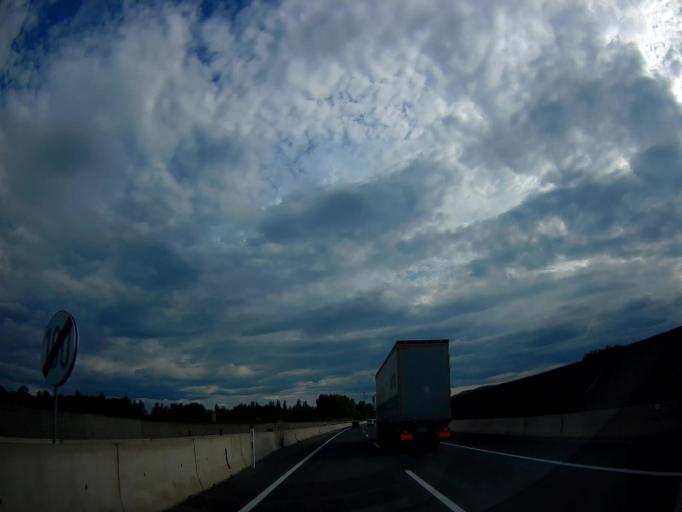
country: AT
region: Lower Austria
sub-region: Politischer Bezirk Krems
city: Grafenegg
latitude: 48.4029
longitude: 15.7388
